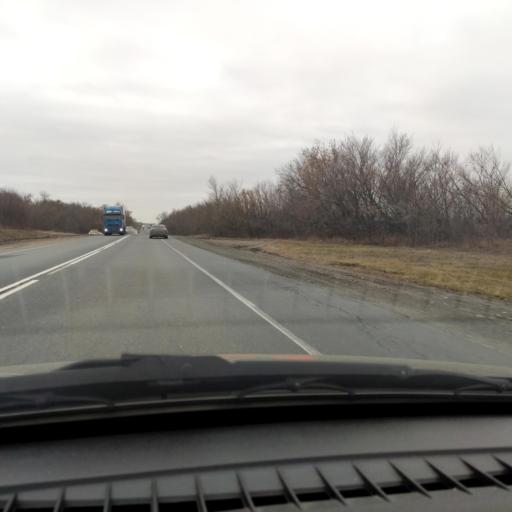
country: RU
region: Samara
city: Zhigulevsk
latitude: 53.3564
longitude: 49.4559
